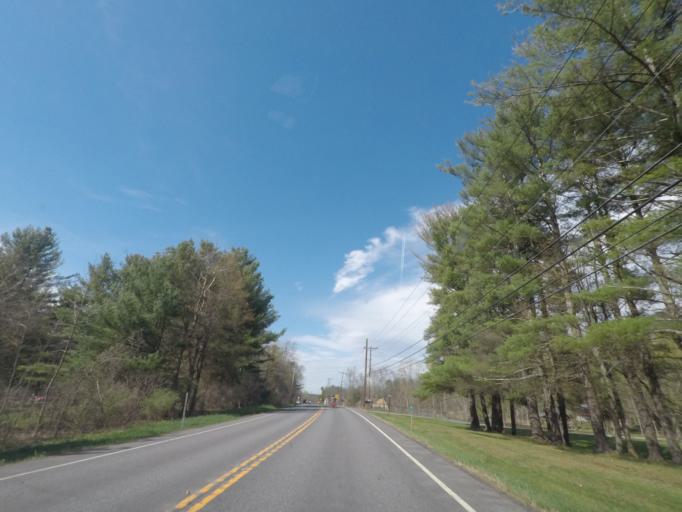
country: US
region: New York
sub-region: Greene County
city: Cairo
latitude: 42.3741
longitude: -74.0357
